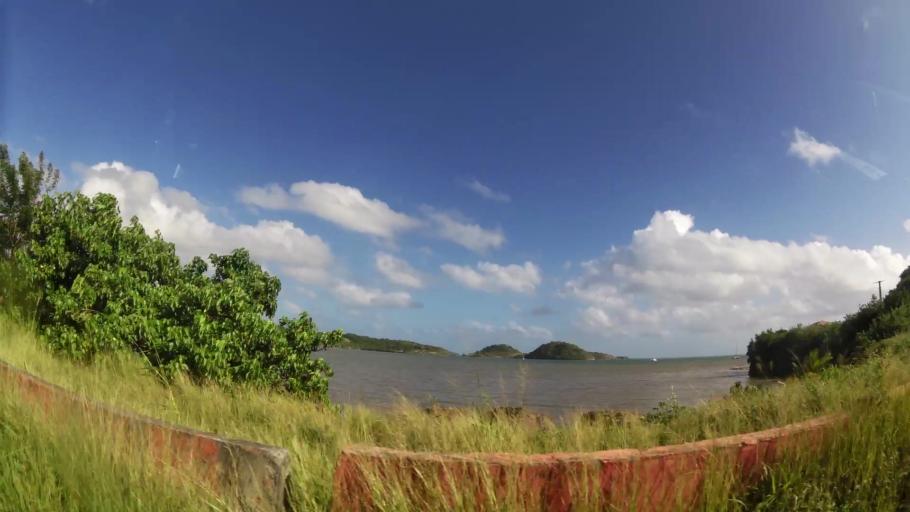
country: MQ
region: Martinique
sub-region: Martinique
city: Le Francois
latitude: 14.6193
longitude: -60.8942
